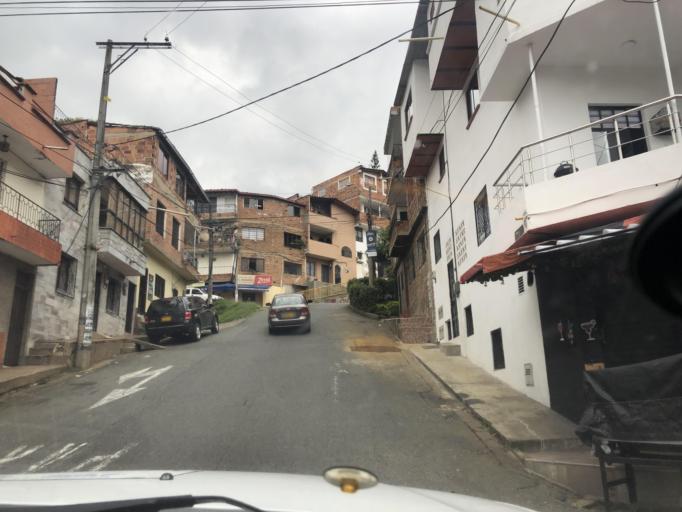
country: CO
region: Antioquia
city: Bello
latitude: 6.3356
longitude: -75.5619
